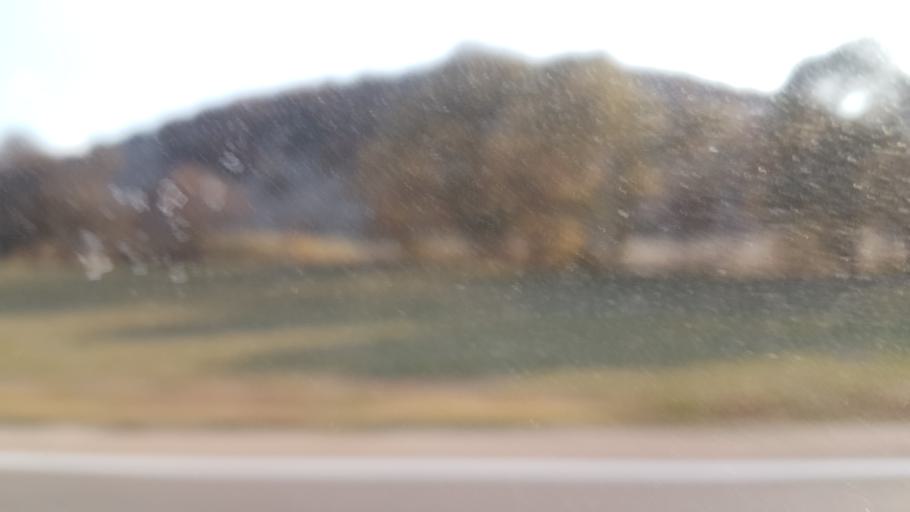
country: TR
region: Eskisehir
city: Kirka
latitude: 39.3572
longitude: 30.5900
